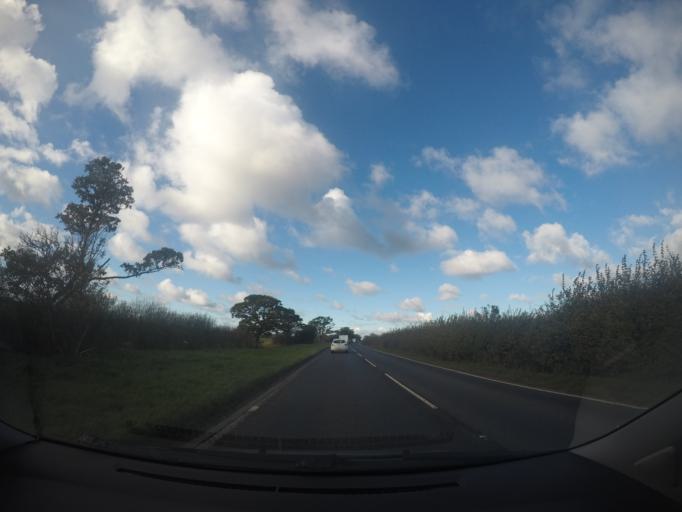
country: GB
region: England
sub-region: City of York
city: Askham Richard
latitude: 53.9936
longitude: -1.2441
